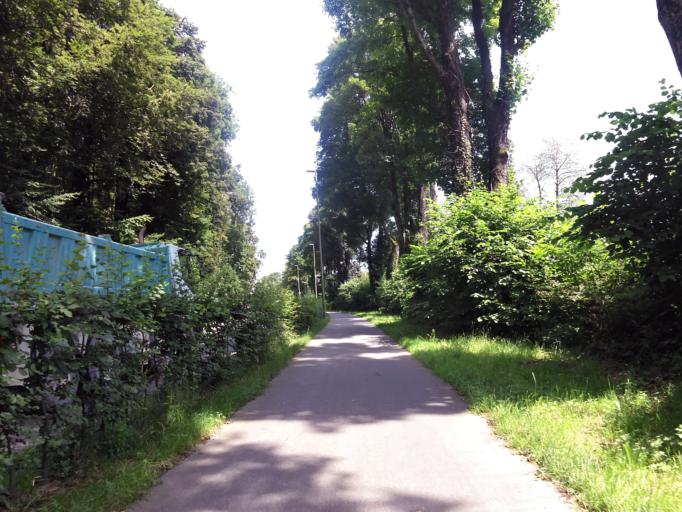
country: DE
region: Baden-Wuerttemberg
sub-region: Tuebingen Region
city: Friedrichshafen
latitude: 47.6591
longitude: 9.4380
